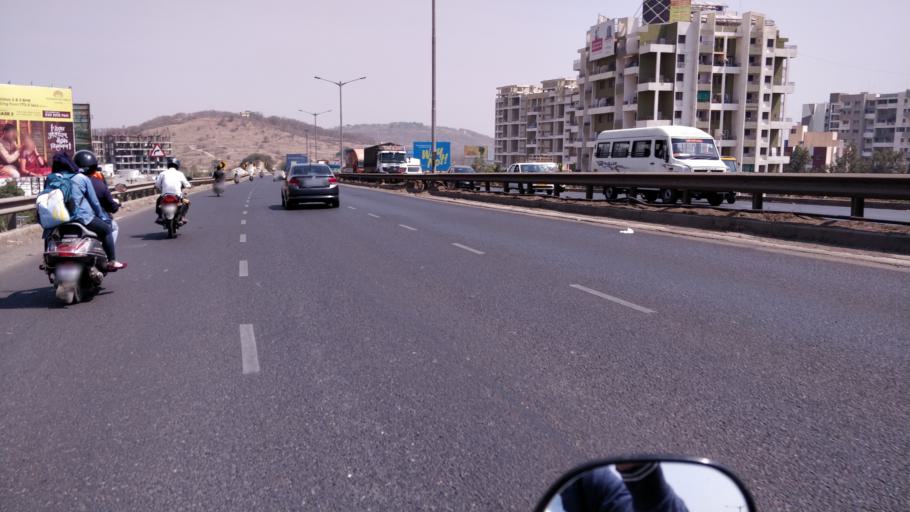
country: IN
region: Maharashtra
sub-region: Pune Division
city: Kharakvasla
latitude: 18.5200
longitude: 73.7690
